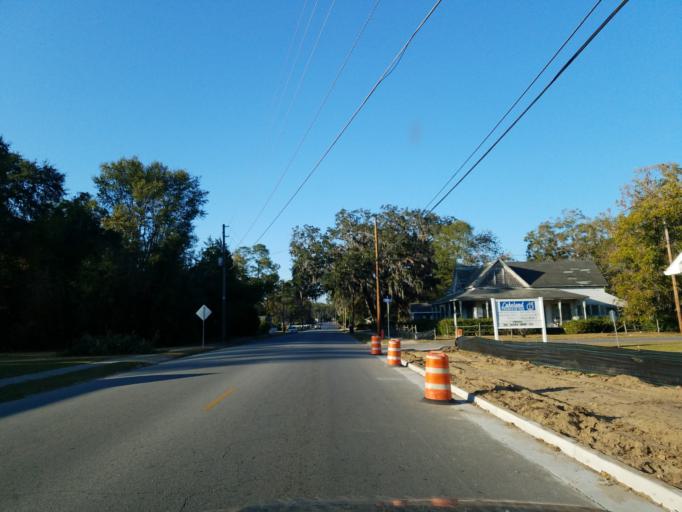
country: US
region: Georgia
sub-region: Lanier County
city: Lakeland
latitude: 31.0372
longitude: -83.0701
